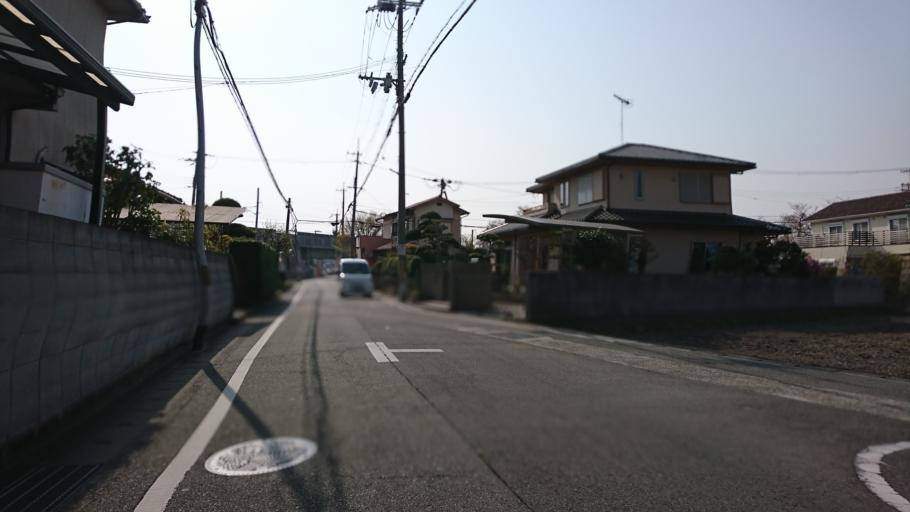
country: JP
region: Hyogo
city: Kakogawacho-honmachi
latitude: 34.7177
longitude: 134.8716
